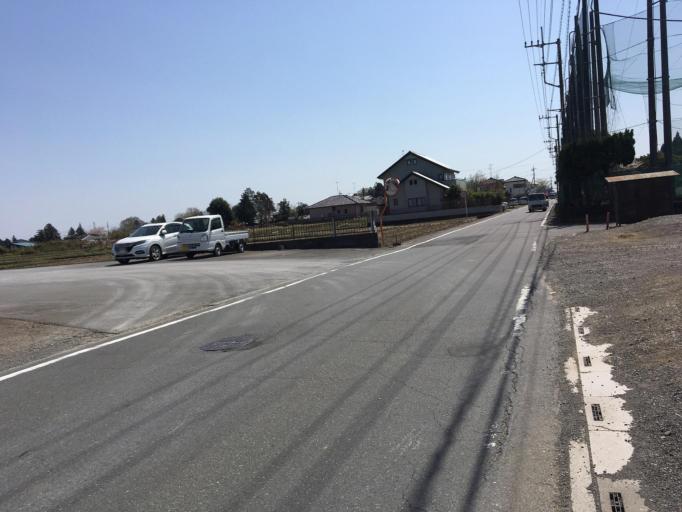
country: JP
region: Saitama
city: Sakado
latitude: 35.9521
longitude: 139.3513
